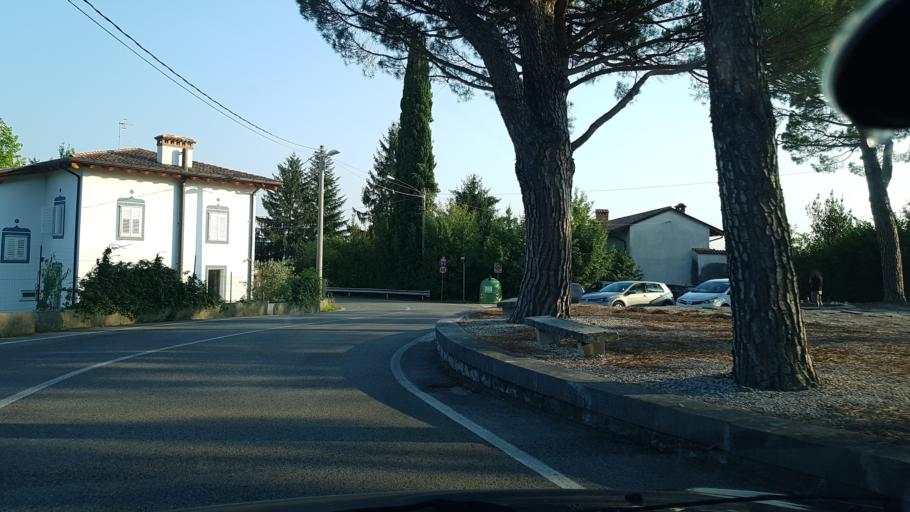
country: IT
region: Friuli Venezia Giulia
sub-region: Provincia di Gorizia
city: Gorizia
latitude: 45.9684
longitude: 13.6152
